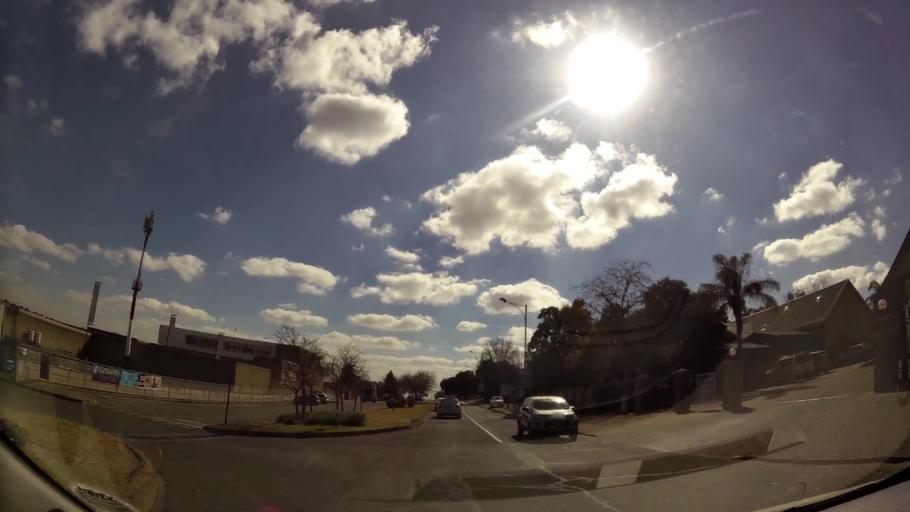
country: ZA
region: Gauteng
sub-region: West Rand District Municipality
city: Krugersdorp
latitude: -26.0969
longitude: 27.8038
